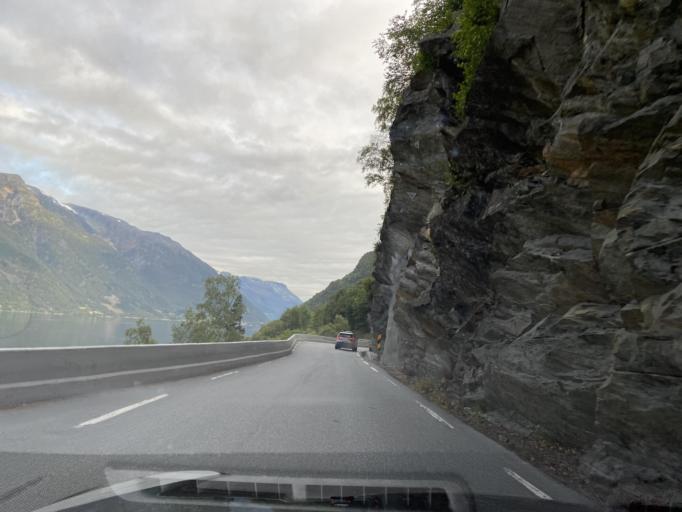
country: NO
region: Hordaland
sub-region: Odda
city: Odda
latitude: 60.1512
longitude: 6.5713
